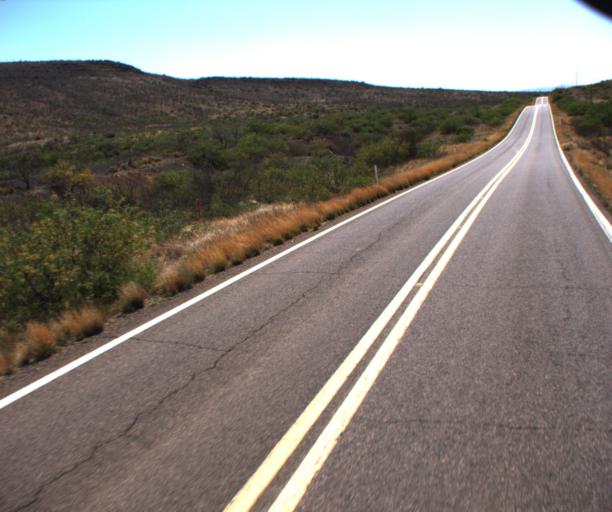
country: US
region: Arizona
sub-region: Cochise County
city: Douglas
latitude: 31.4726
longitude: -109.3899
